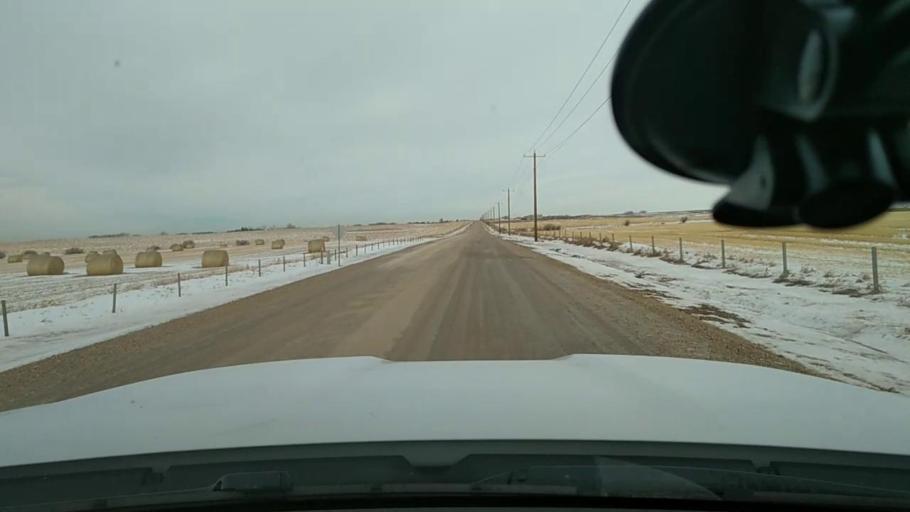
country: CA
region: Alberta
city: Airdrie
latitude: 51.2141
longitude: -113.9118
